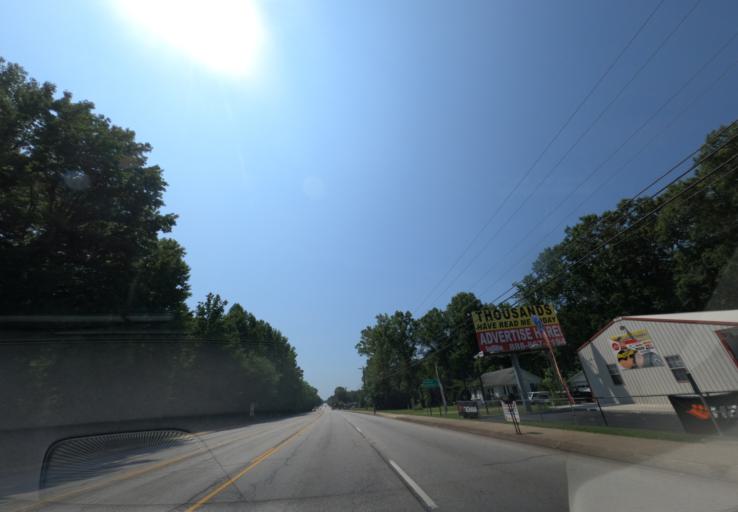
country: US
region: South Carolina
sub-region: Greenwood County
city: Greenwood
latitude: 34.1516
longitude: -82.1384
